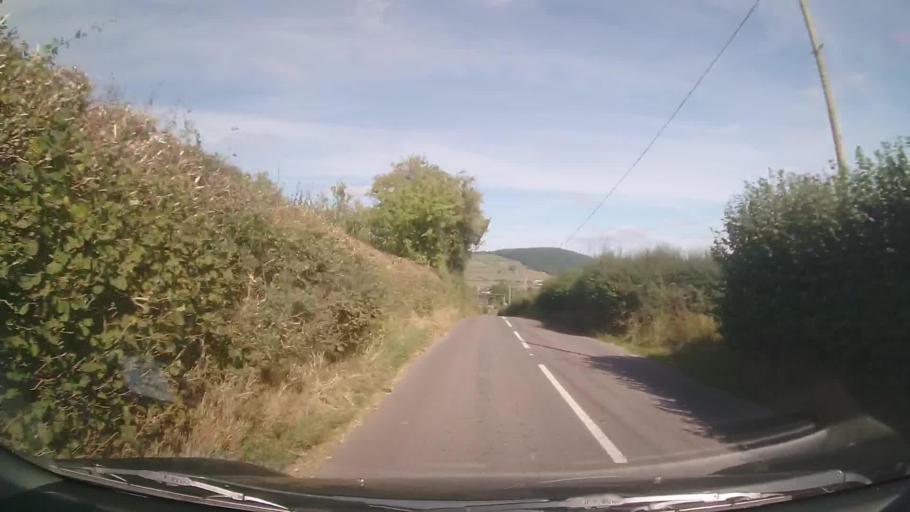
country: GB
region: England
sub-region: Shropshire
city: Acton
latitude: 52.4160
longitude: -3.0371
